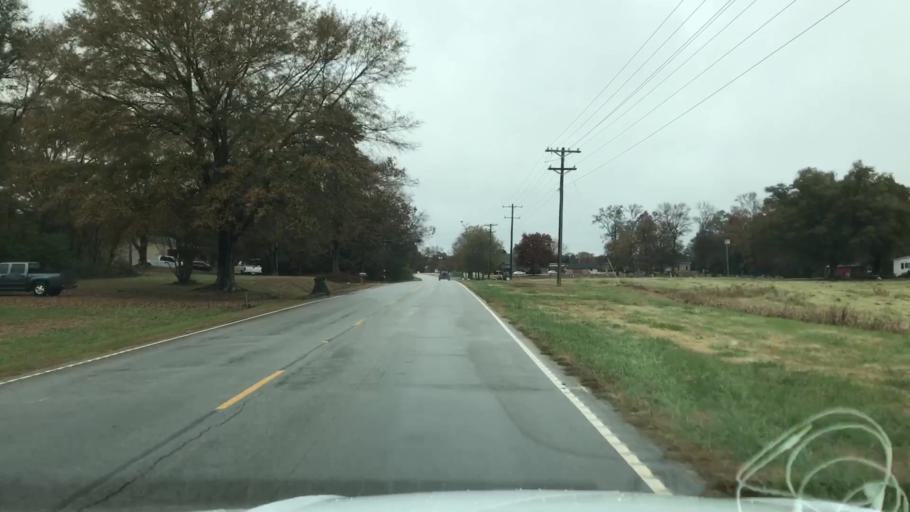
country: US
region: South Carolina
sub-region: Spartanburg County
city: Roebuck
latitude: 34.8003
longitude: -81.9161
